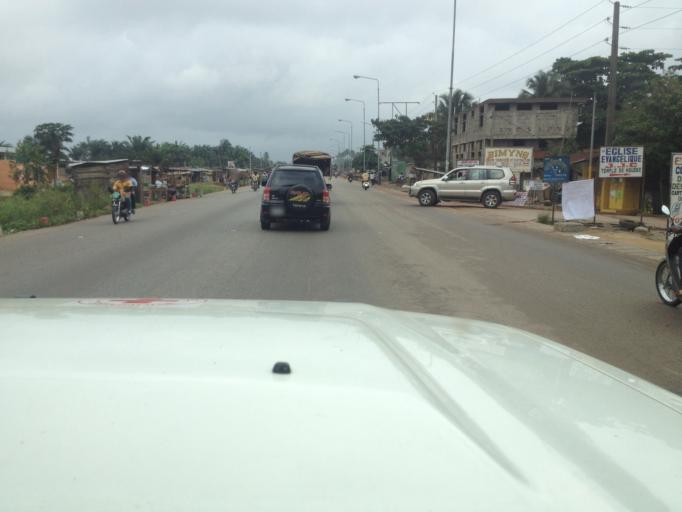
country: BJ
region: Queme
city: Porto-Novo
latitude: 6.4335
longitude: 2.6251
